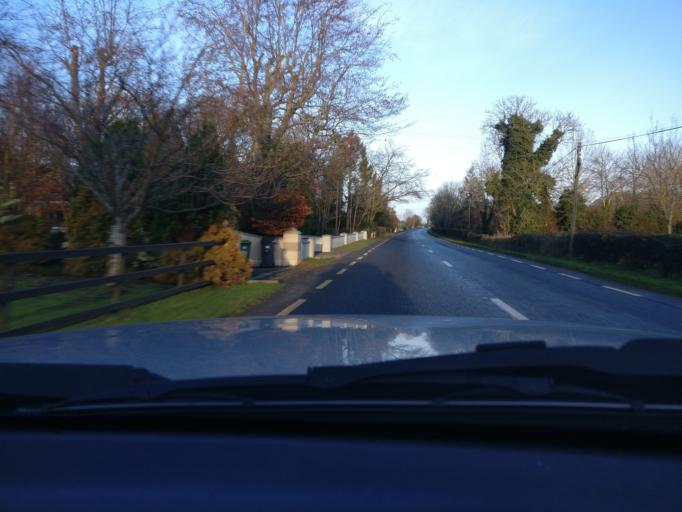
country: IE
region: Leinster
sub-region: Lu
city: Ardee
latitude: 53.8205
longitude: -6.6445
